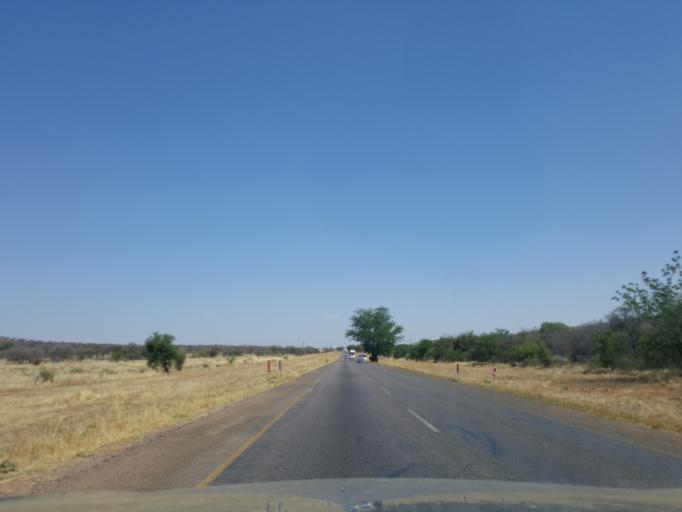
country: BW
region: South East
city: Lobatse
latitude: -25.1612
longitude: 25.6888
